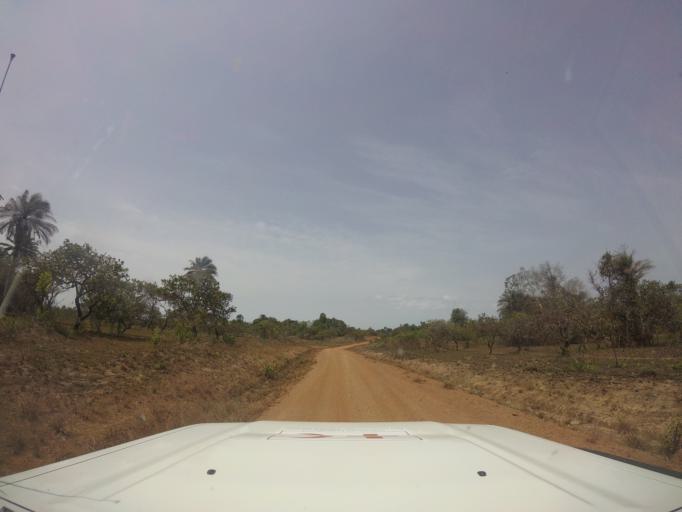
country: LR
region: Grand Cape Mount
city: Robertsport
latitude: 6.9256
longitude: -11.3613
